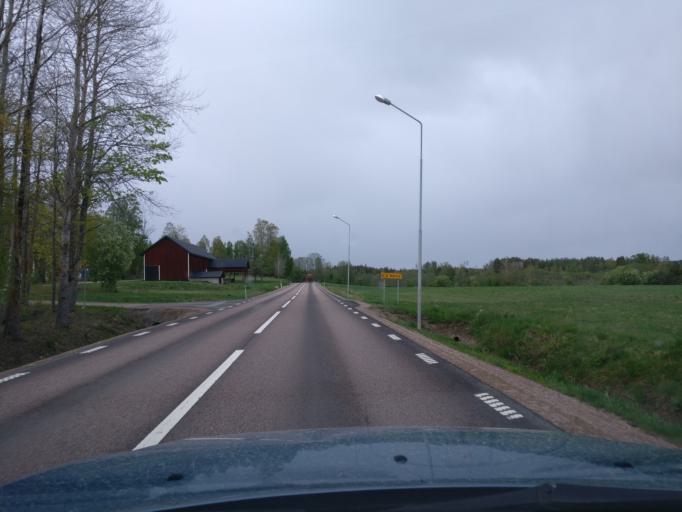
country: SE
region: Vaermland
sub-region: Forshaga Kommun
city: Deje
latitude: 59.6438
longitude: 13.4431
